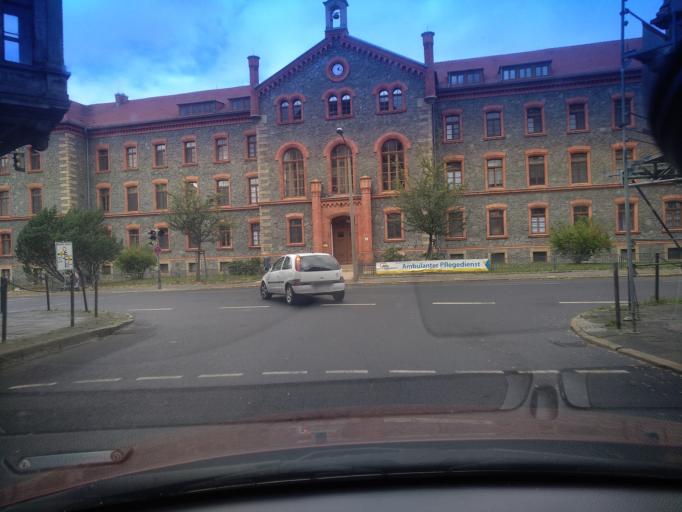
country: DE
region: Saxony
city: Goerlitz
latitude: 51.1516
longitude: 14.9801
